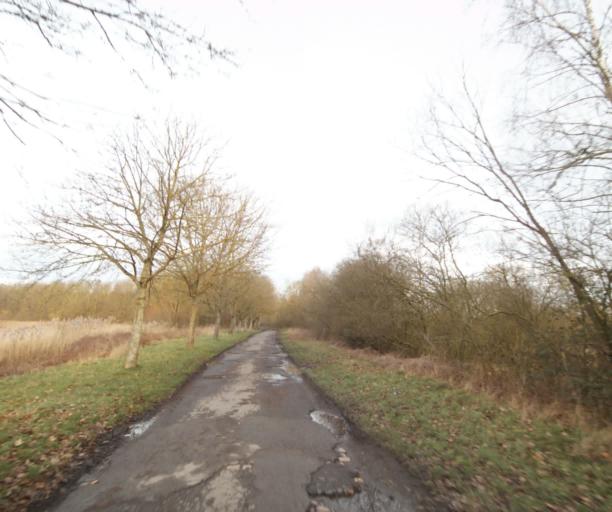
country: BE
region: Wallonia
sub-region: Province du Hainaut
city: Bernissart
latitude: 50.4675
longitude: 3.6196
